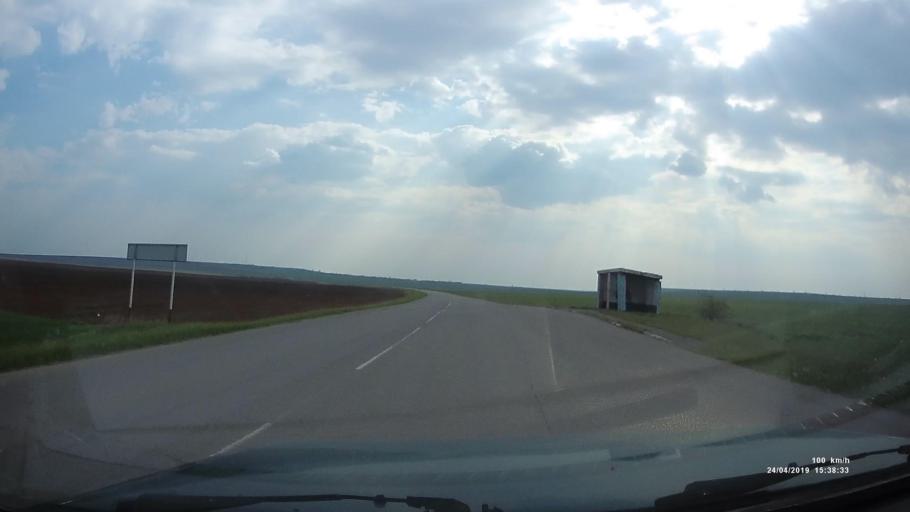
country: RU
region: Kalmykiya
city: Yashalta
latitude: 46.5967
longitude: 42.8259
